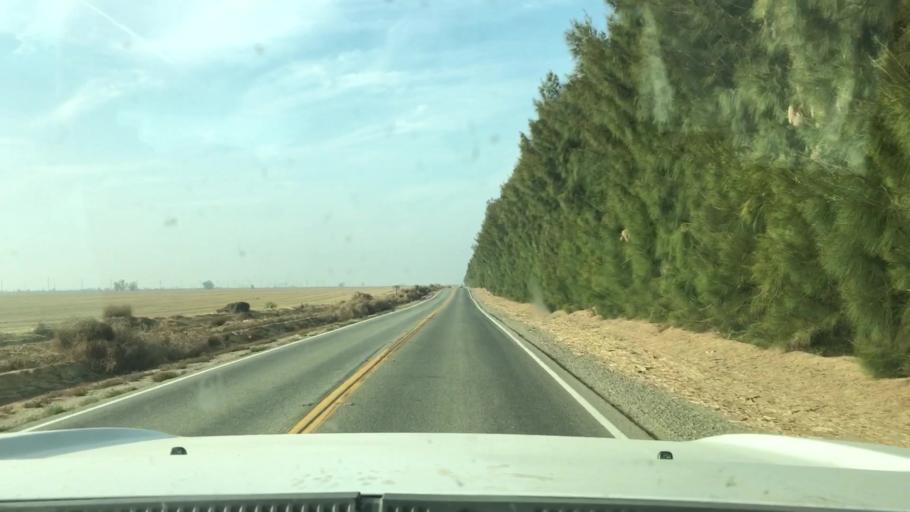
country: US
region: California
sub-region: Kern County
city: Lost Hills
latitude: 35.5004
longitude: -119.7404
